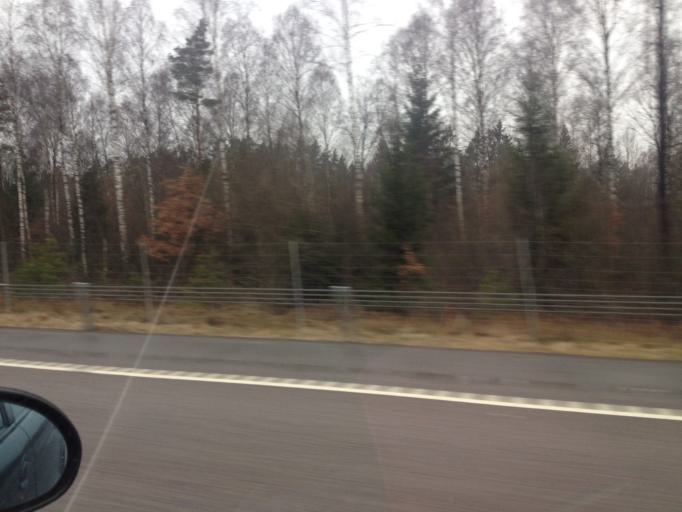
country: SE
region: Kronoberg
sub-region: Markaryds Kommun
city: Markaryd
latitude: 56.4370
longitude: 13.5801
